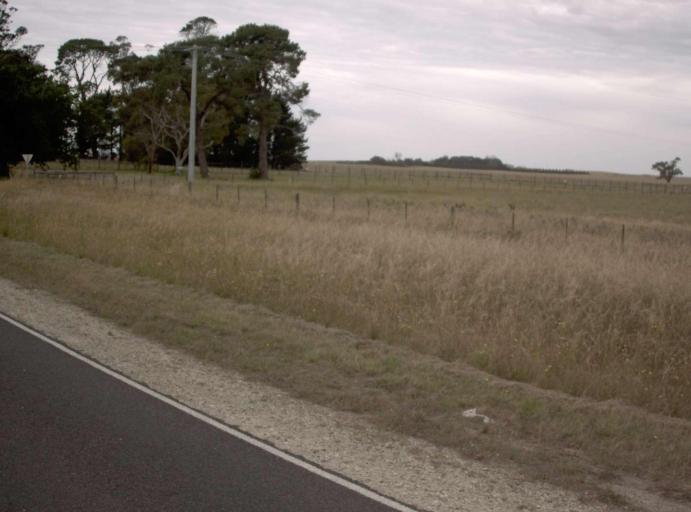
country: AU
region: Victoria
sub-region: Wellington
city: Sale
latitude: -38.1762
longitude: 147.2054
